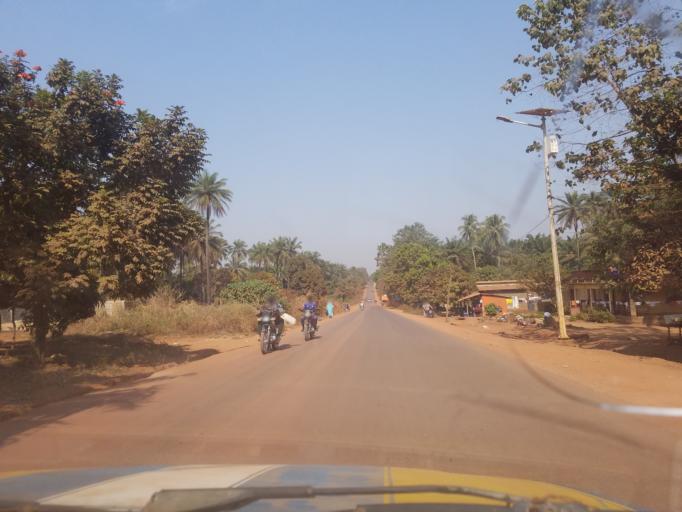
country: GN
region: Boke
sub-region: Boke Prefecture
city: Sangueya
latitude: 10.8009
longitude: -14.3926
